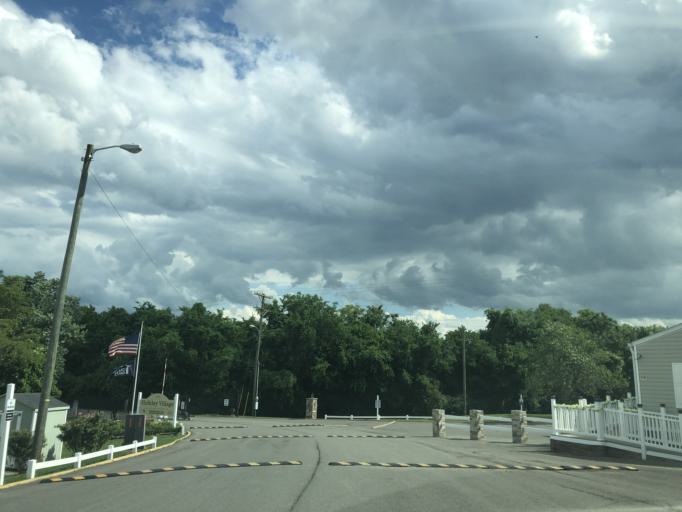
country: US
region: Tennessee
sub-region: Davidson County
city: Nashville
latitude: 36.2096
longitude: -86.7708
